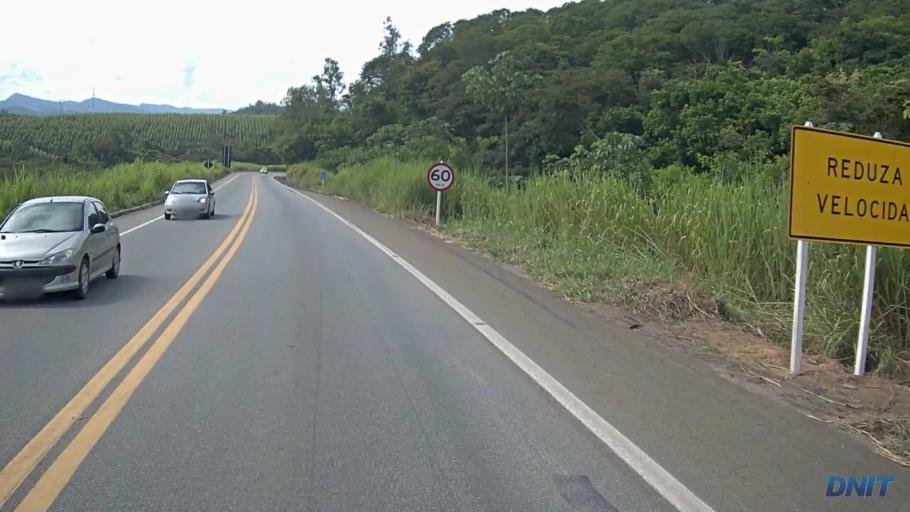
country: BR
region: Minas Gerais
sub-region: Ipaba
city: Ipaba
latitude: -19.3777
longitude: -42.4613
